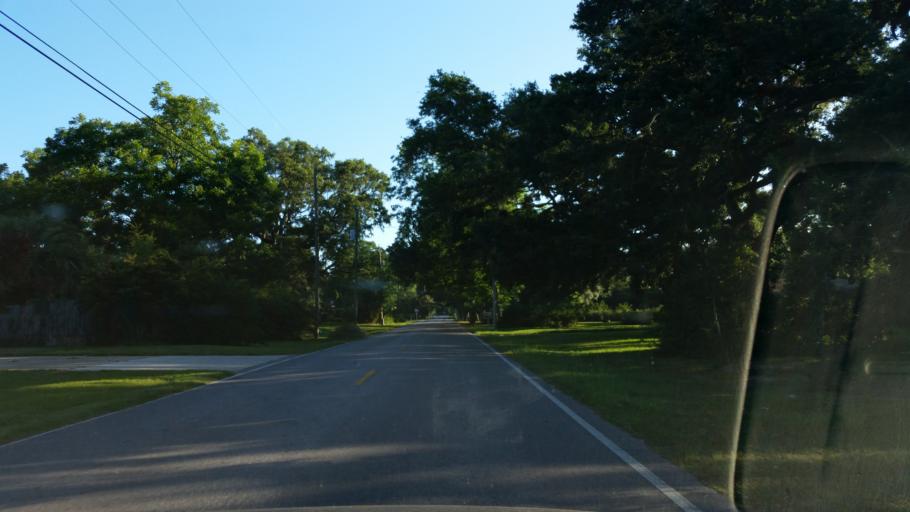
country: US
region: Florida
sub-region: Escambia County
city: Bellview
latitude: 30.4638
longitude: -87.3157
